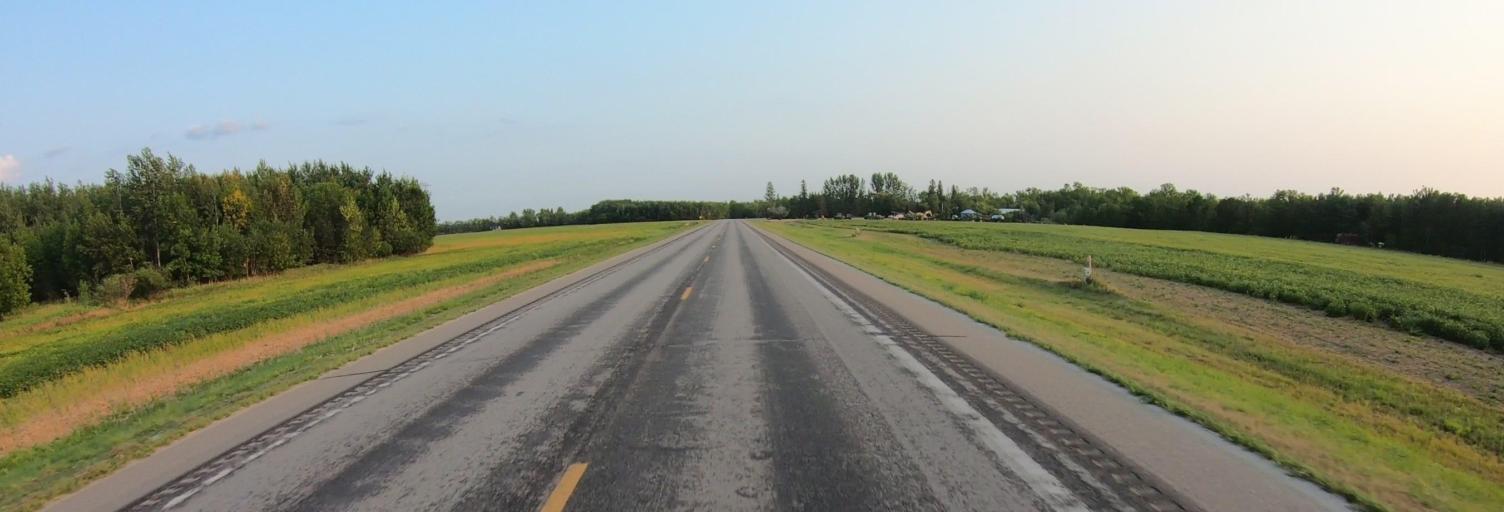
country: US
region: Minnesota
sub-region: Roseau County
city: Warroad
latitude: 48.8862
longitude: -95.3201
